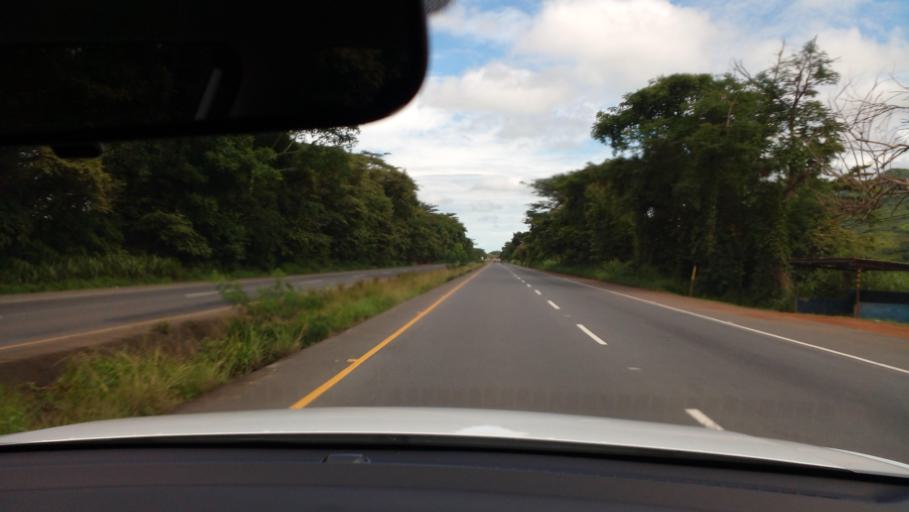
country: PA
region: Cocle
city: El Cano
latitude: 8.3753
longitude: -80.5297
